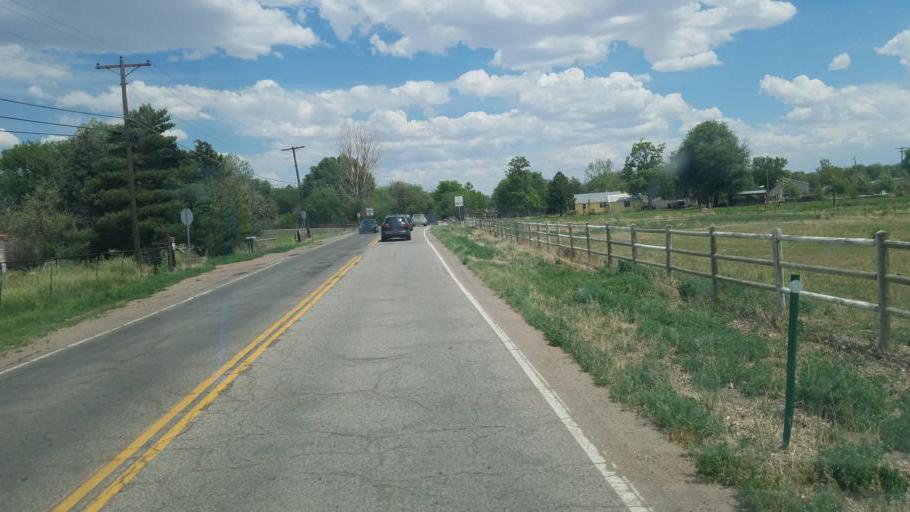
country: US
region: Colorado
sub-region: Fremont County
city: Florence
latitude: 38.4022
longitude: -105.1380
